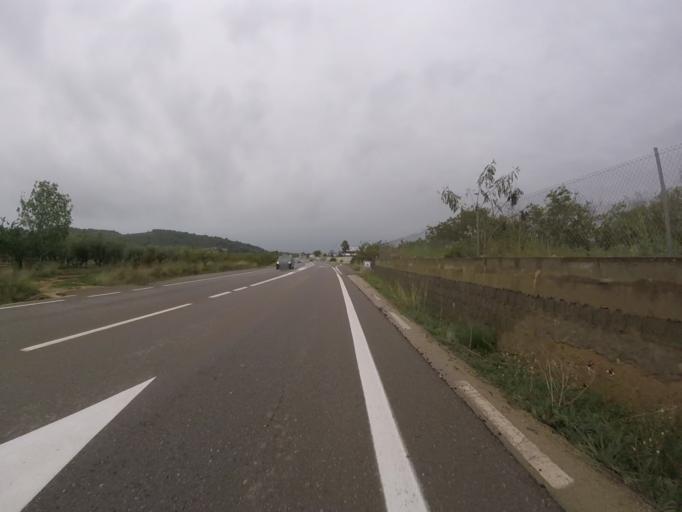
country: ES
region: Valencia
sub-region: Provincia de Castello
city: Alcoceber
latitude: 40.2579
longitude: 0.2443
